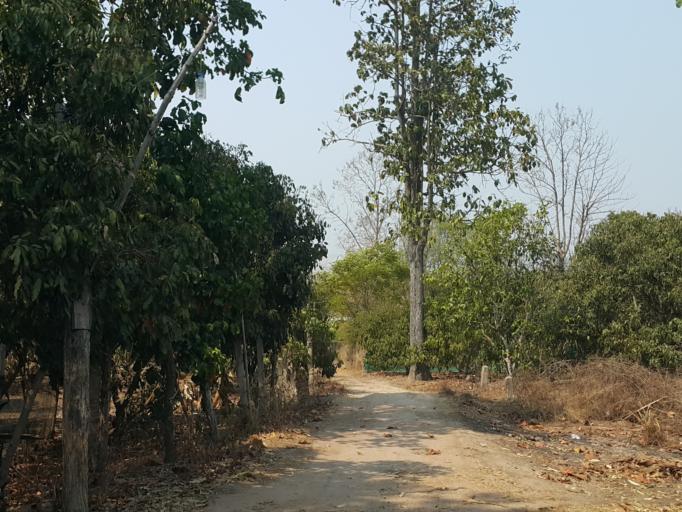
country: TH
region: Chiang Mai
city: Mae On
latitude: 18.7072
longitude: 99.1979
